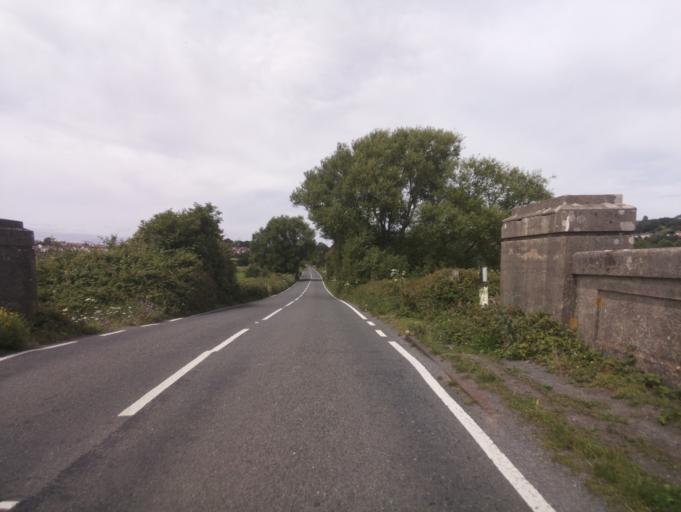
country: GB
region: England
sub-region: Somerset
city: Glastonbury
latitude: 51.1349
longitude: -2.7130
